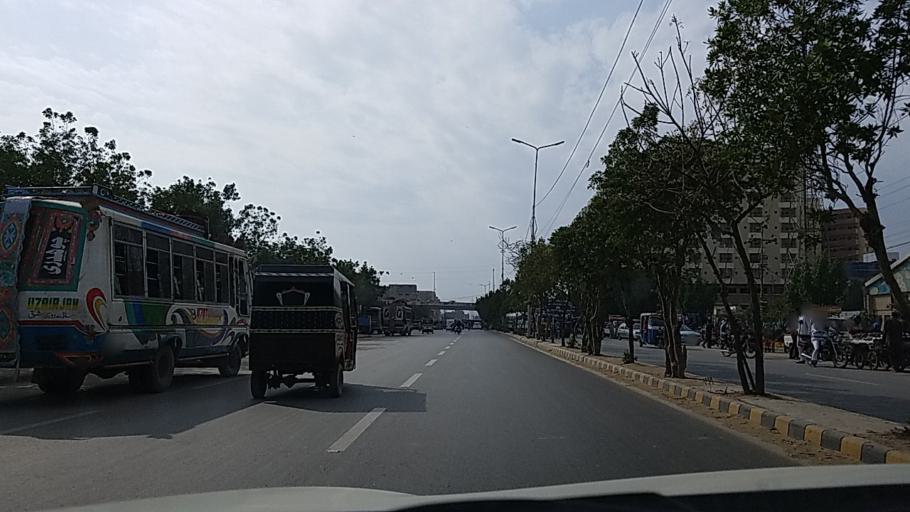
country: PK
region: Sindh
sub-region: Karachi District
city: Karachi
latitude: 24.8175
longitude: 67.1104
